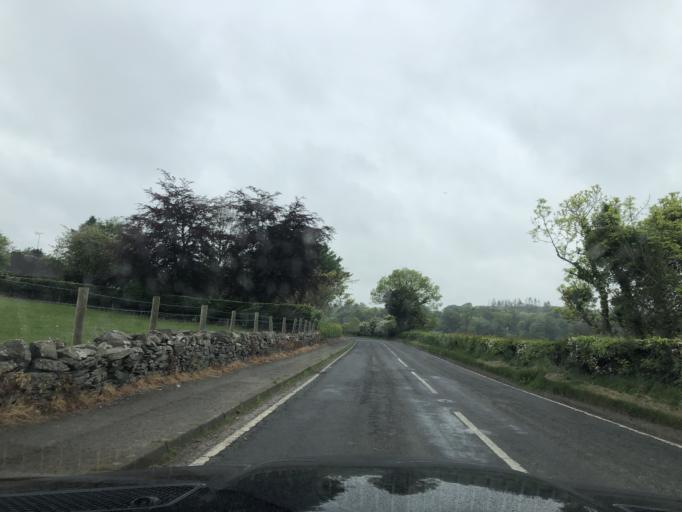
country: GB
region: Northern Ireland
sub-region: Down District
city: Portaferry
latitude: 54.3664
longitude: -5.5625
